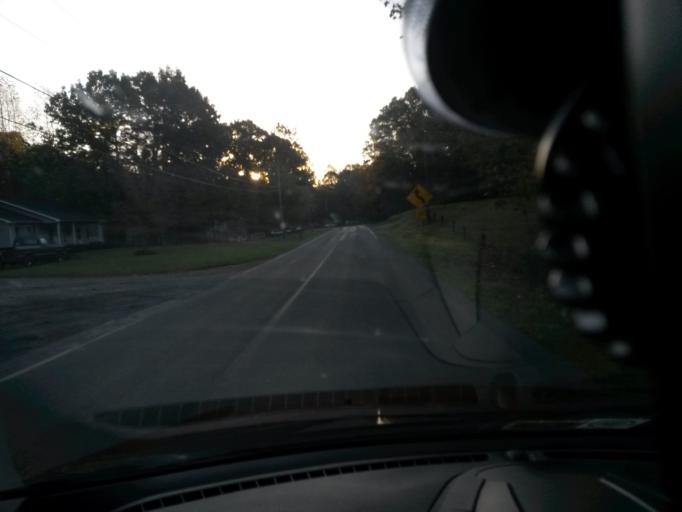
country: US
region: Virginia
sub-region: Roanoke County
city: Narrows
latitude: 37.1599
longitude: -79.8432
